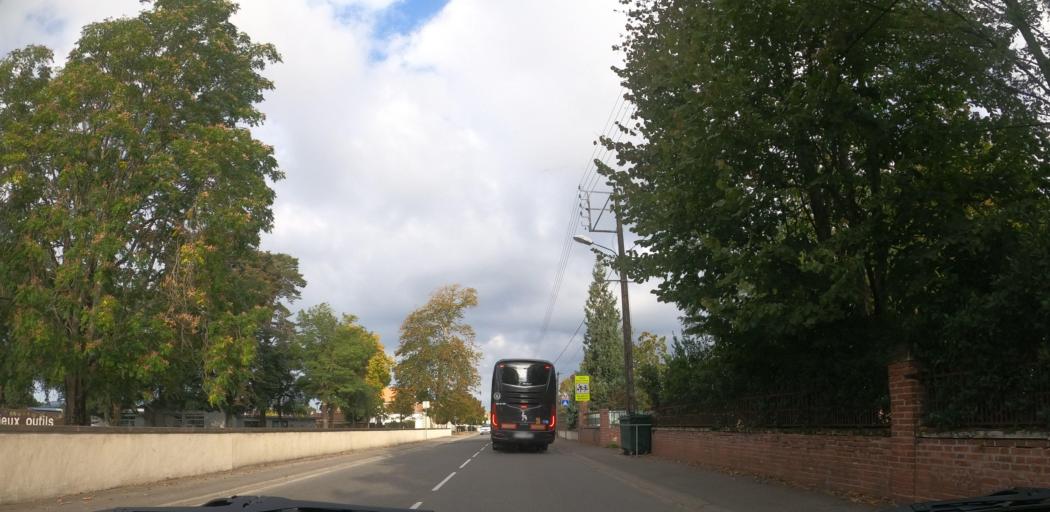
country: FR
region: Aquitaine
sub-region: Departement des Landes
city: Soustons
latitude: 43.7514
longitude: -1.3230
